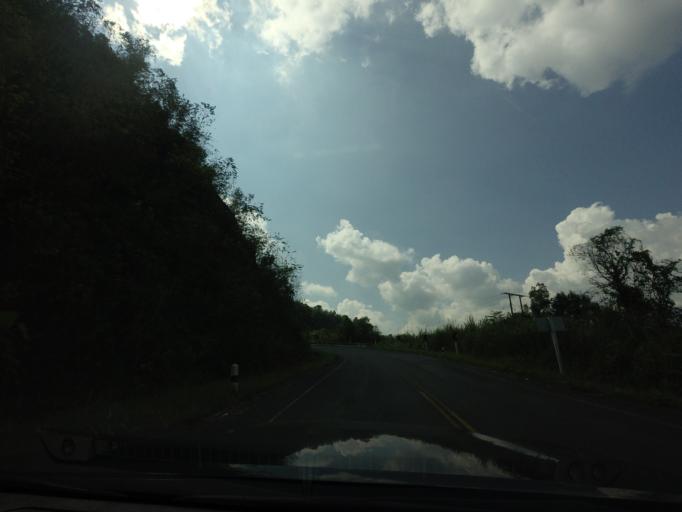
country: TH
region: Nan
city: Bo Kluea
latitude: 19.0691
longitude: 101.1260
